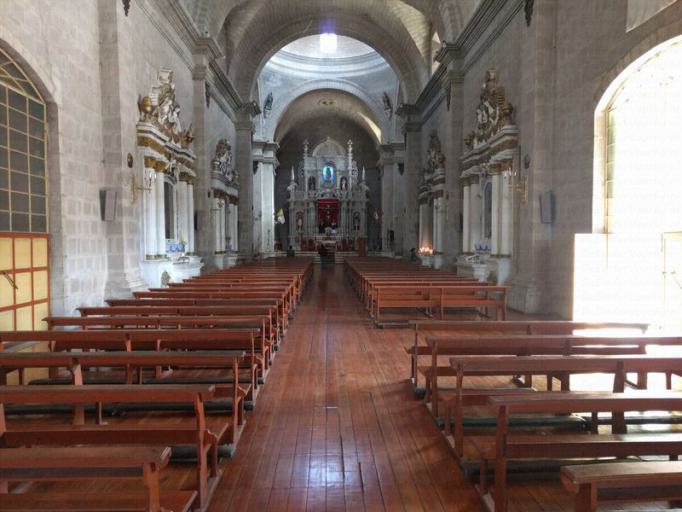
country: PE
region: Puno
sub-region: Provincia de Puno
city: Puno
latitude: -15.8409
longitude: -70.0287
